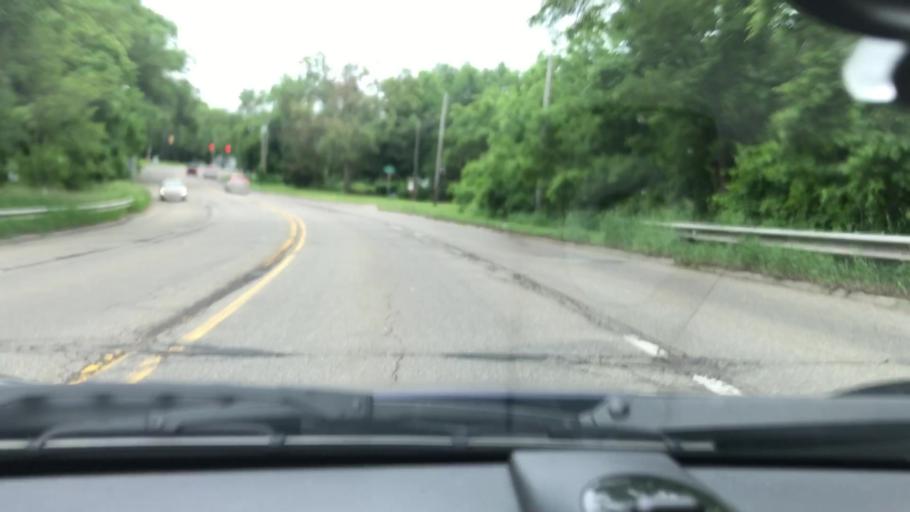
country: US
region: Michigan
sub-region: Calhoun County
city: Springfield
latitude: 42.3560
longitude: -85.2320
